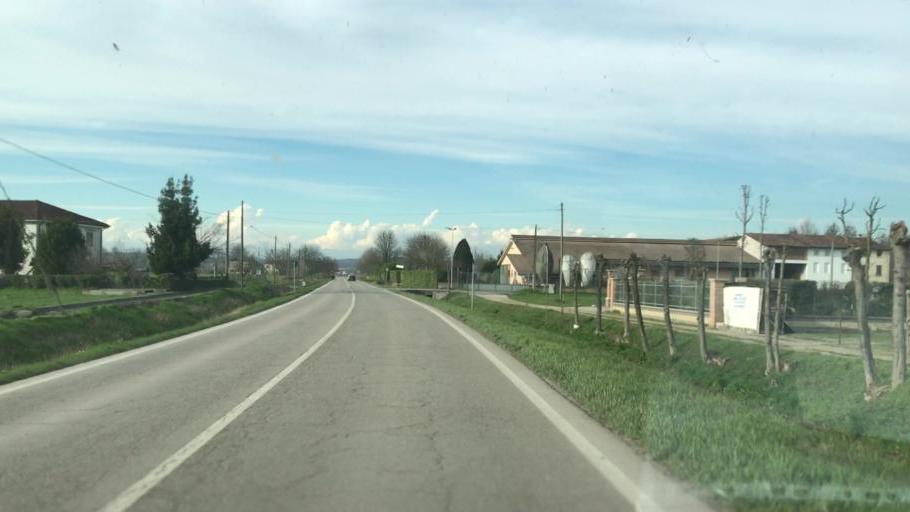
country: IT
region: Lombardy
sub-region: Provincia di Mantova
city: Cerlongo
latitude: 45.2864
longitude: 10.6573
